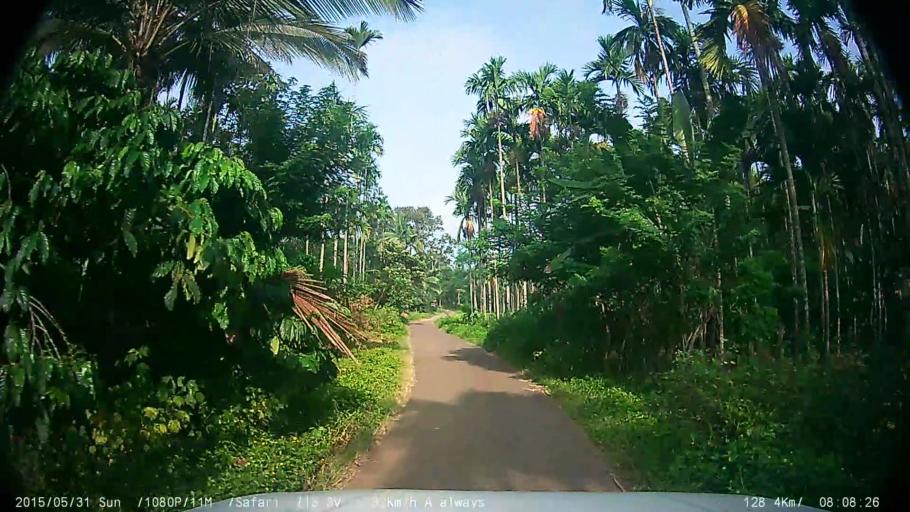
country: IN
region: Kerala
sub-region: Wayanad
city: Kalpetta
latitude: 11.6407
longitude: 76.0252
